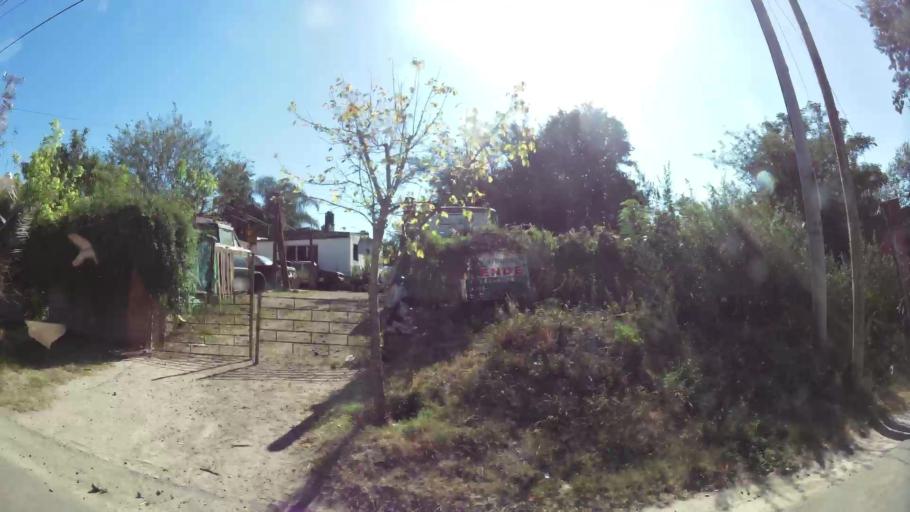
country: AR
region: Cordoba
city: La Calera
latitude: -31.3560
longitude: -64.3142
